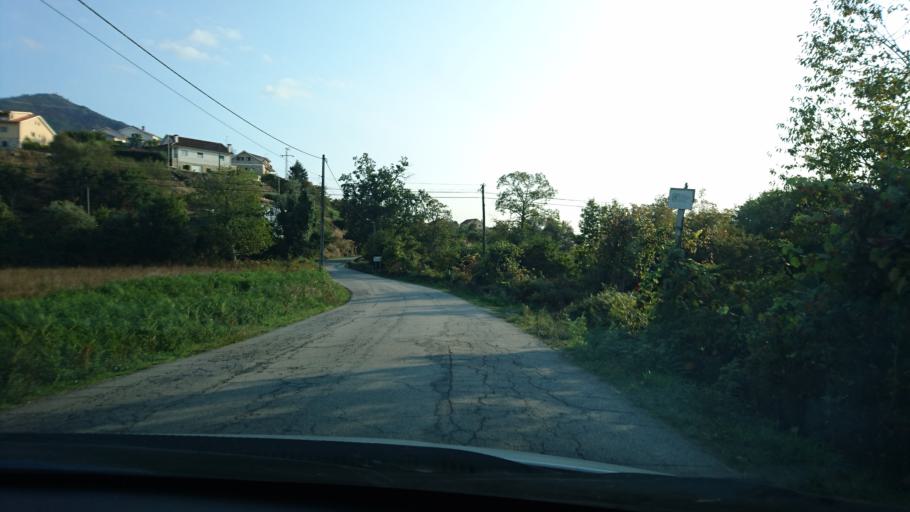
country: PT
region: Vila Real
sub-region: Mondim de Basto
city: Mondim de Basto
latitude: 41.4426
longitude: -7.9262
